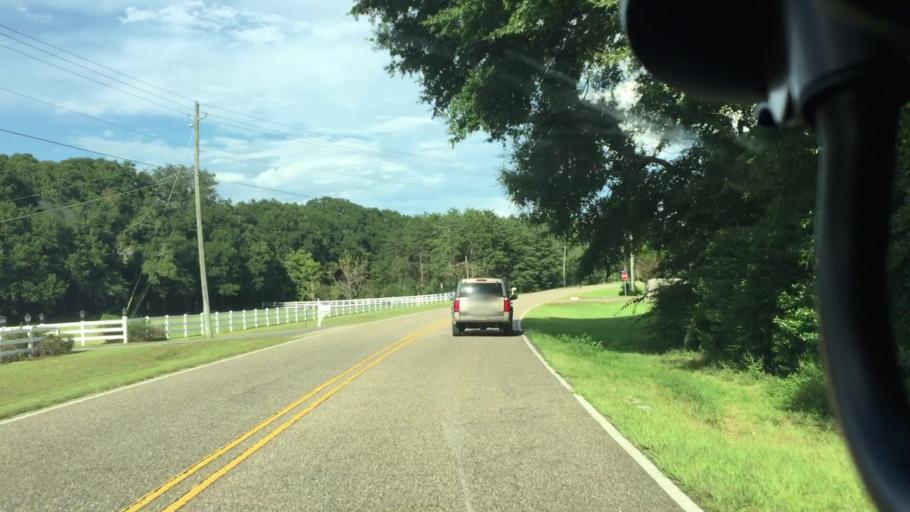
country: US
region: Alabama
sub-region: Coffee County
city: Enterprise
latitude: 31.3689
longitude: -85.8438
